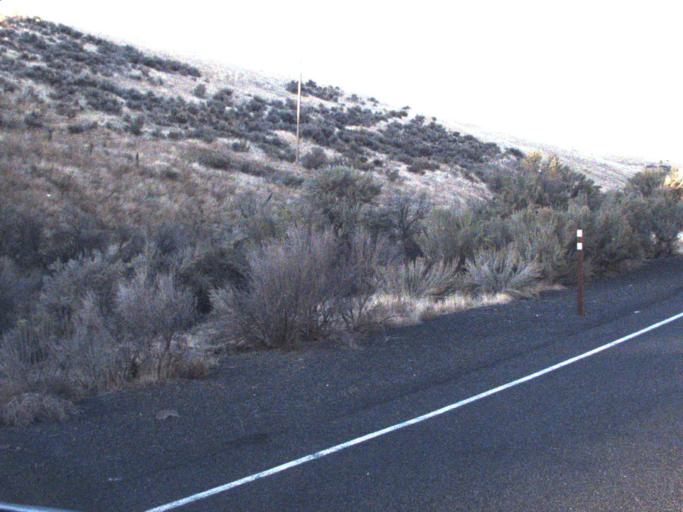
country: US
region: Washington
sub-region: Franklin County
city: Connell
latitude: 46.6790
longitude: -118.5386
